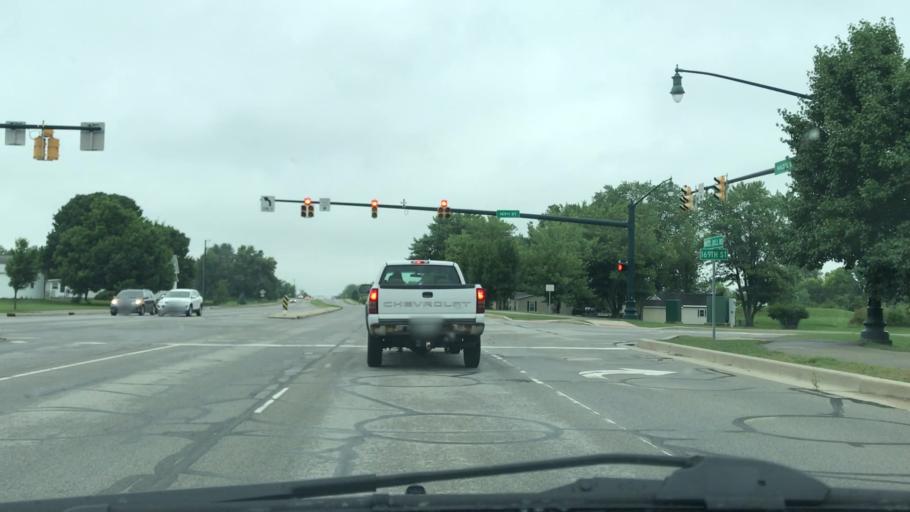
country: US
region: Indiana
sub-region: Hamilton County
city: Westfield
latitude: 40.0327
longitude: -86.0706
